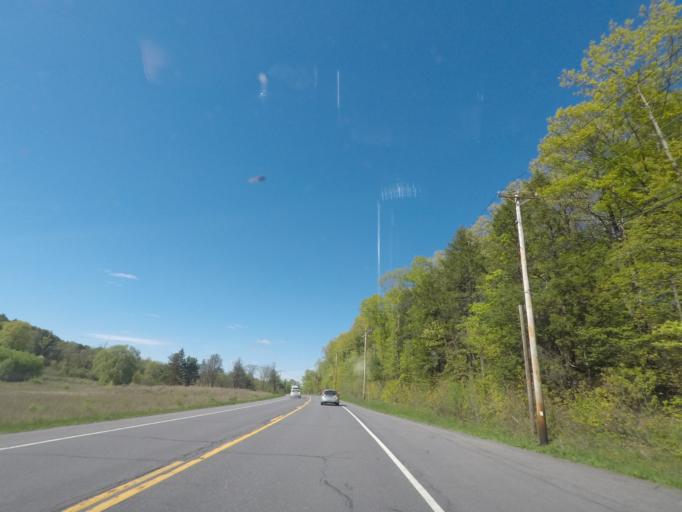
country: US
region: New York
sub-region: Albany County
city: Ravena
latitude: 42.4327
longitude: -73.8149
